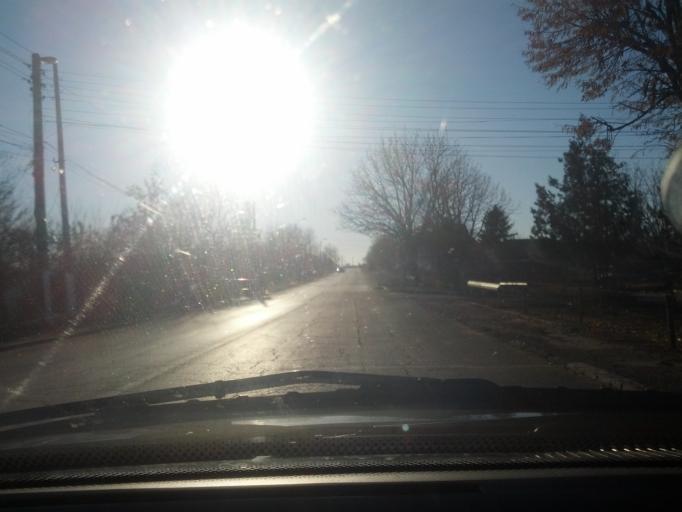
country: BG
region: Vratsa
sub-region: Obshtina Miziya
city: Miziya
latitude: 43.7055
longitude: 23.8276
